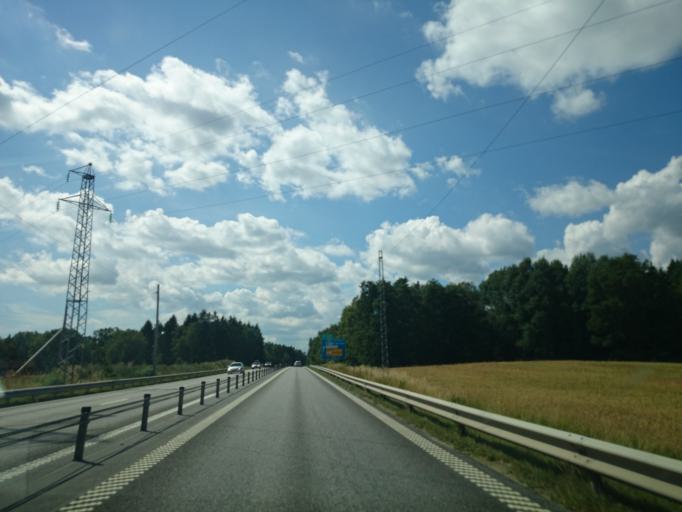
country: SE
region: Kalmar
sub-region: Kalmar Kommun
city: Lindsdal
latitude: 56.7685
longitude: 16.3235
